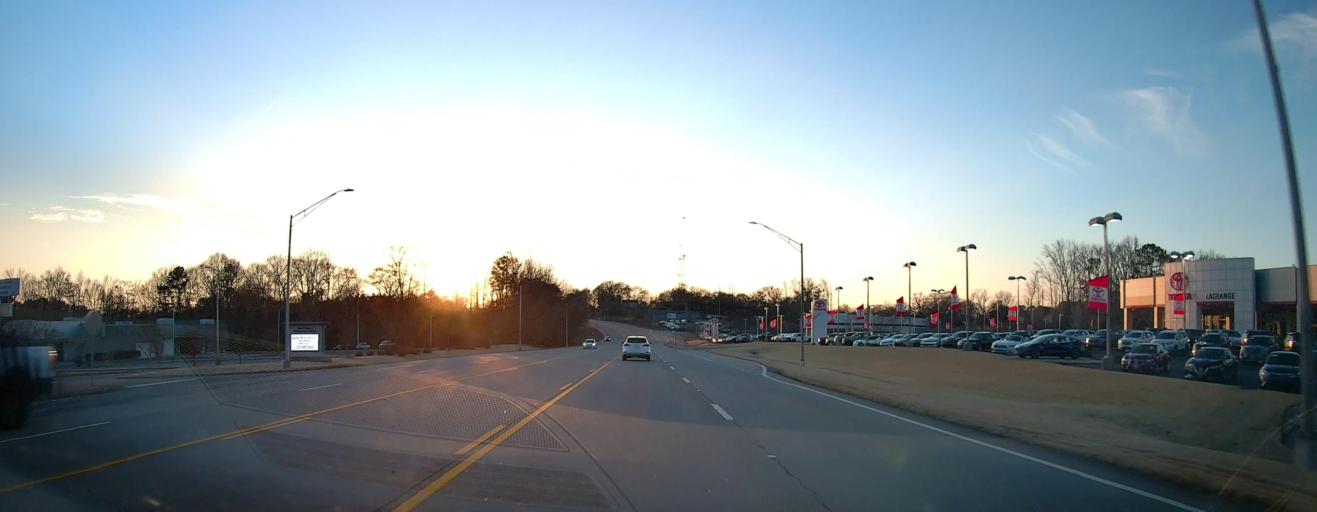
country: US
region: Georgia
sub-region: Troup County
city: La Grange
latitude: 33.0412
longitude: -84.9997
